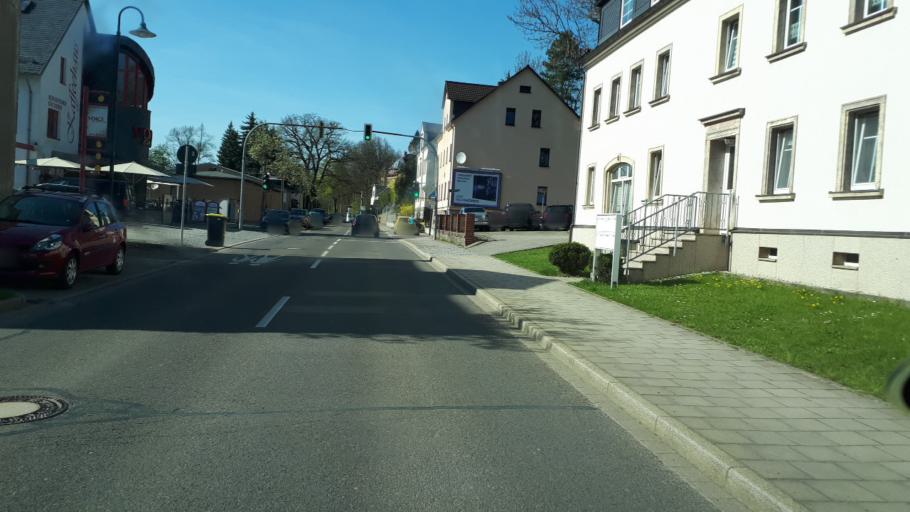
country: DE
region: Saxony
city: Chemnitz
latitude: 50.7874
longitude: 12.9512
